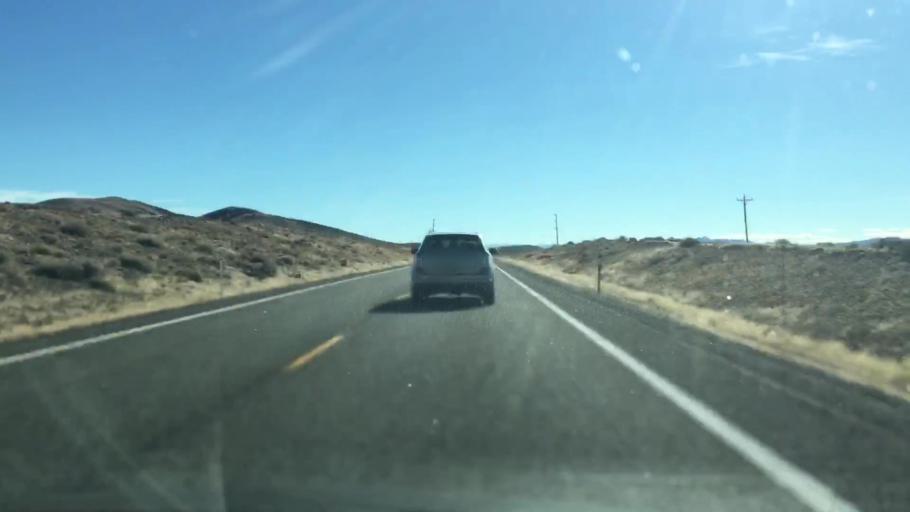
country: US
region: Nevada
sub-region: Lyon County
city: Silver Springs
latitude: 39.1995
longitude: -119.2133
